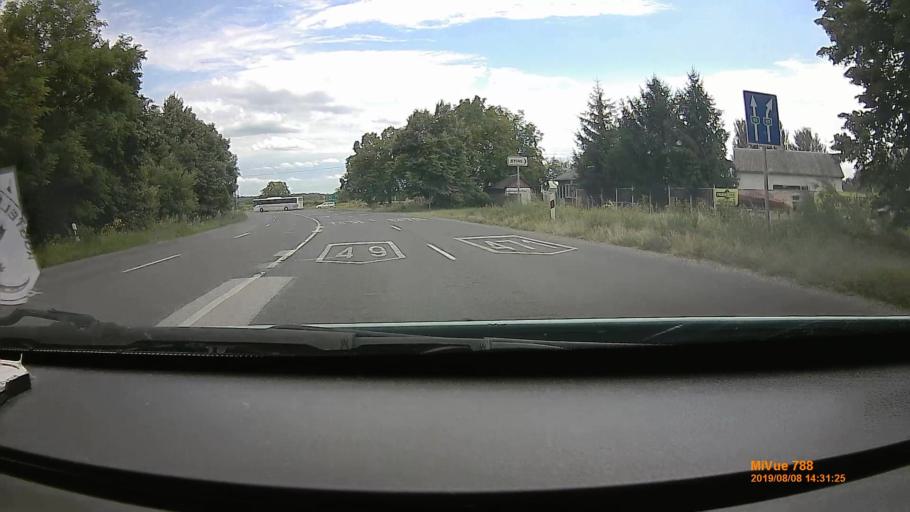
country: HU
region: Szabolcs-Szatmar-Bereg
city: Mateszalka
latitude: 47.9417
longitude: 22.3270
